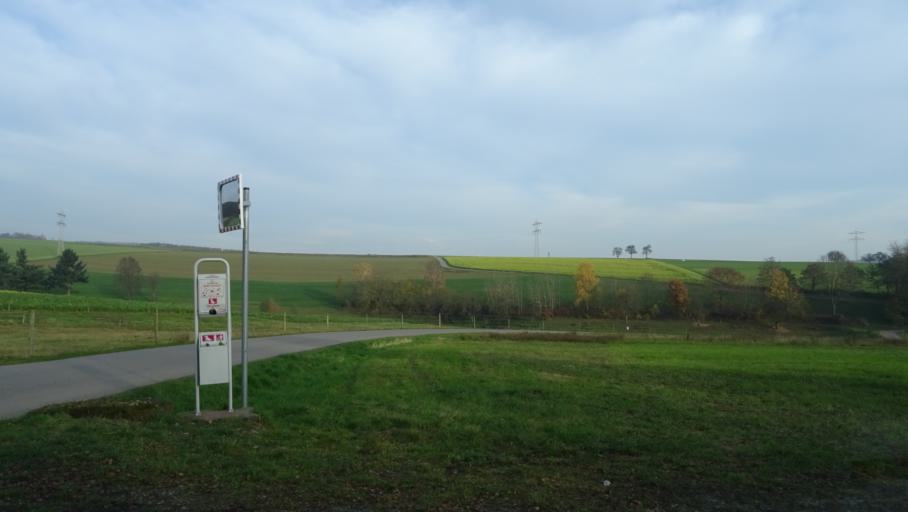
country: DE
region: Baden-Wuerttemberg
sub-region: Karlsruhe Region
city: Neckargerach
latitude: 49.4127
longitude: 9.0775
